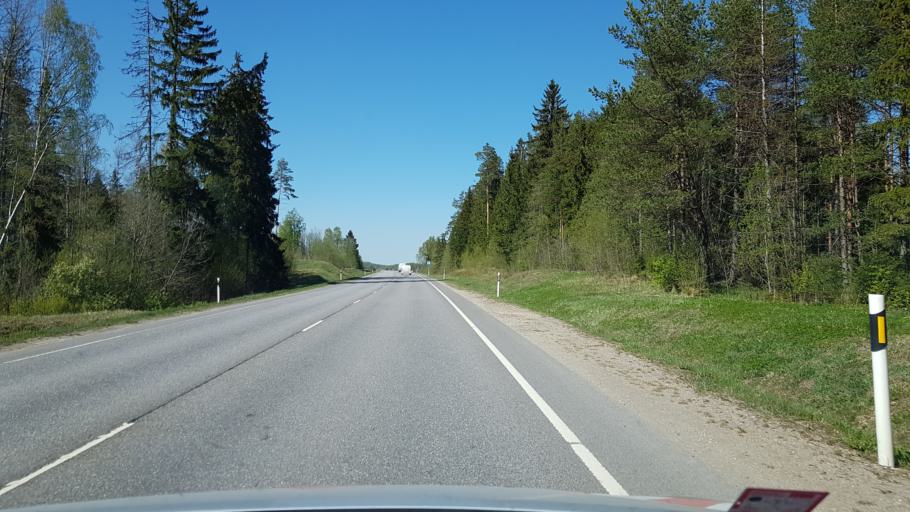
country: EE
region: Tartu
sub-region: UElenurme vald
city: Ulenurme
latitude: 58.0796
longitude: 26.7354
